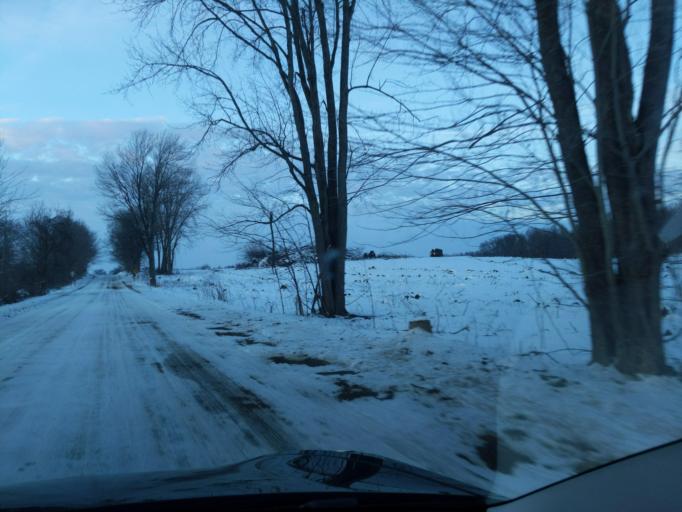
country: US
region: Michigan
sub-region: Ingham County
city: Williamston
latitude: 42.5683
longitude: -84.3129
